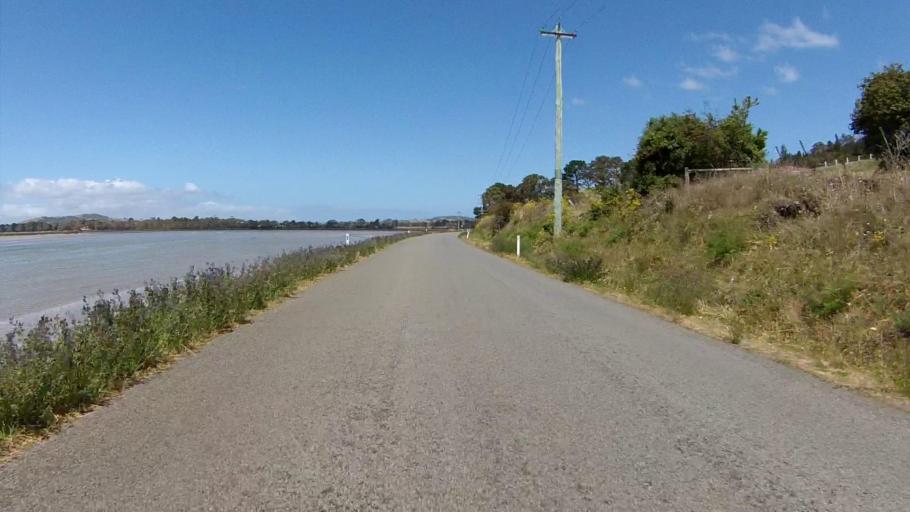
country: AU
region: Tasmania
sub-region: Clarence
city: Lauderdale
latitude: -42.9220
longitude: 147.4805
